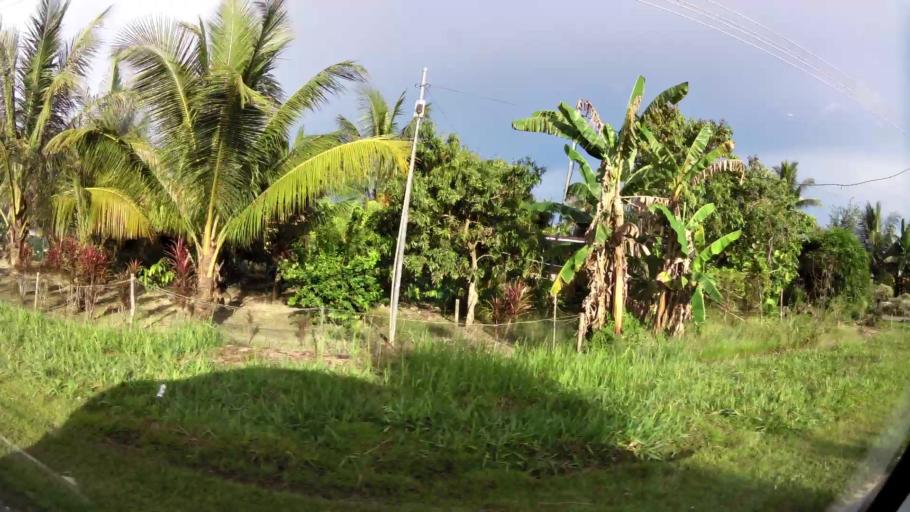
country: BN
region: Brunei and Muara
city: Bandar Seri Begawan
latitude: 4.9605
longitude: 115.0197
